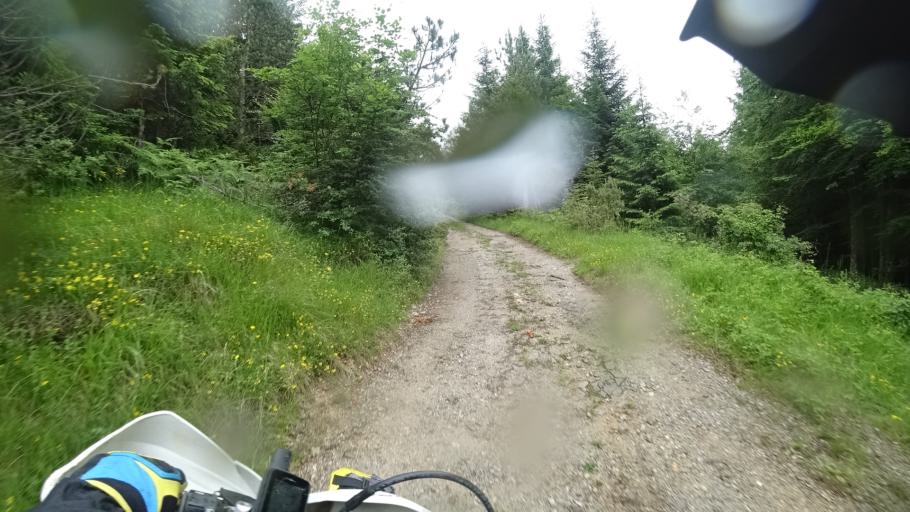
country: HR
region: Primorsko-Goranska
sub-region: Grad Delnice
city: Delnice
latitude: 45.3669
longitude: 14.8948
